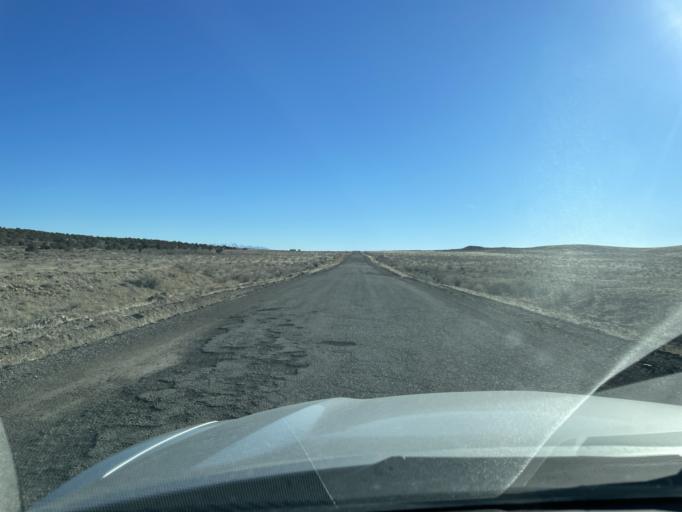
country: US
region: Colorado
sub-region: Mesa County
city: Loma
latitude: 39.1878
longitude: -109.1267
